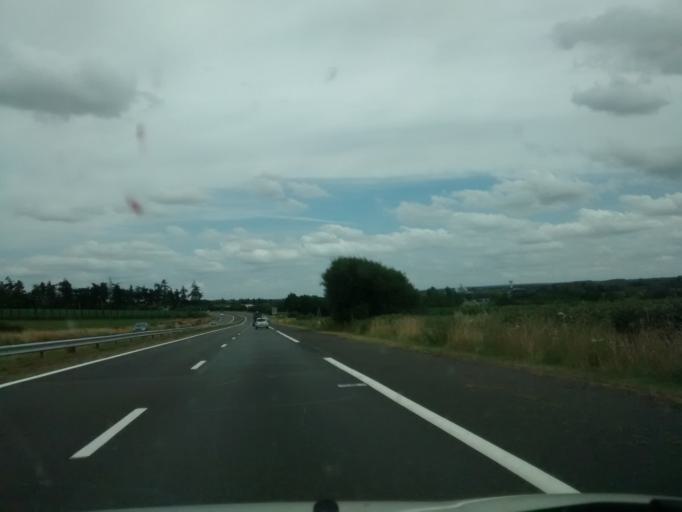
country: FR
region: Brittany
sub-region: Departement d'Ille-et-Vilaine
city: Montauban-de-Bretagne
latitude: 48.2126
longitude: -2.0868
